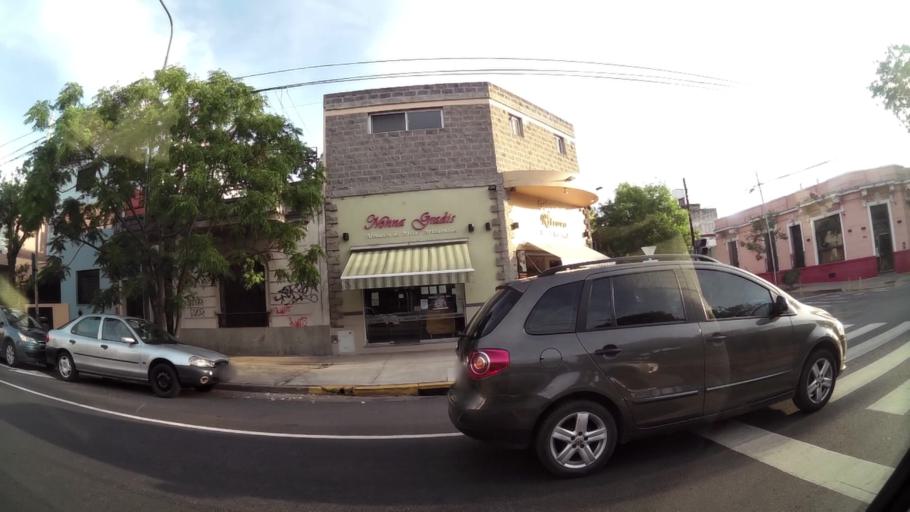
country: AR
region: Buenos Aires F.D.
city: Buenos Aires
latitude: -34.6328
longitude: -58.4280
